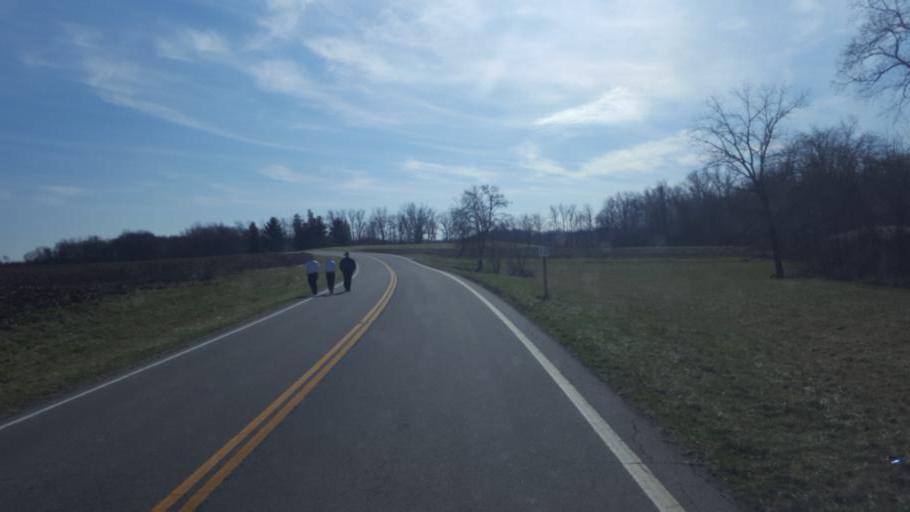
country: US
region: Ohio
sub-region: Hardin County
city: Forest
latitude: 40.6942
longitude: -83.3950
